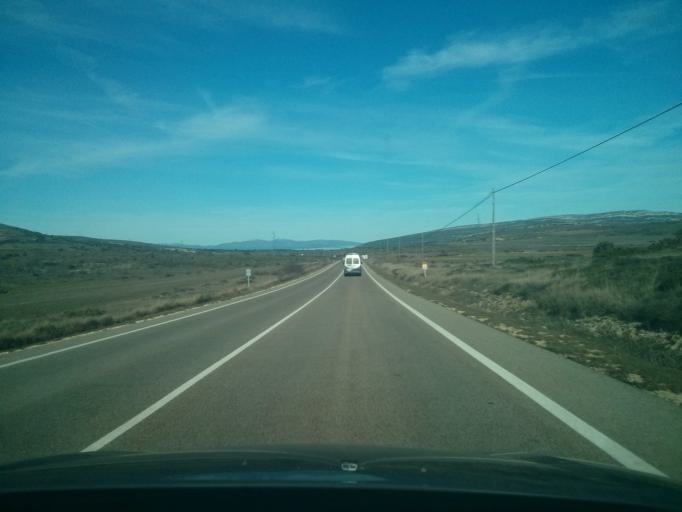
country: ES
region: Castille and Leon
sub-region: Provincia de Burgos
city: Rucandio
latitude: 42.7947
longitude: -3.6189
